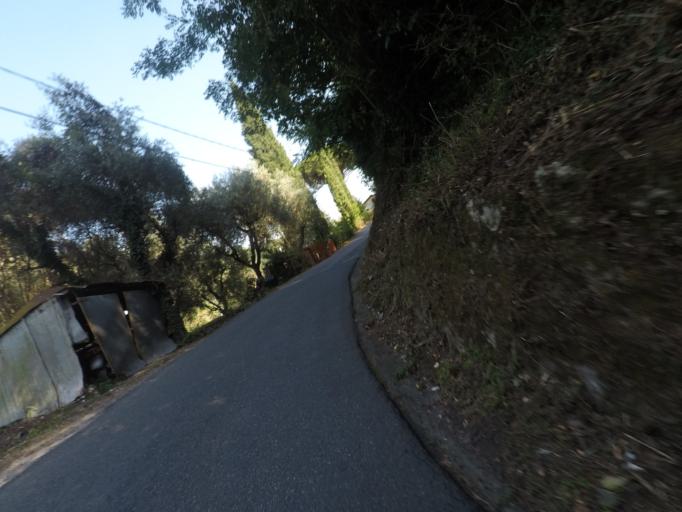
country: IT
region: Tuscany
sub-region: Provincia di Massa-Carrara
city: Carrara
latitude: 44.0788
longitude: 10.0727
